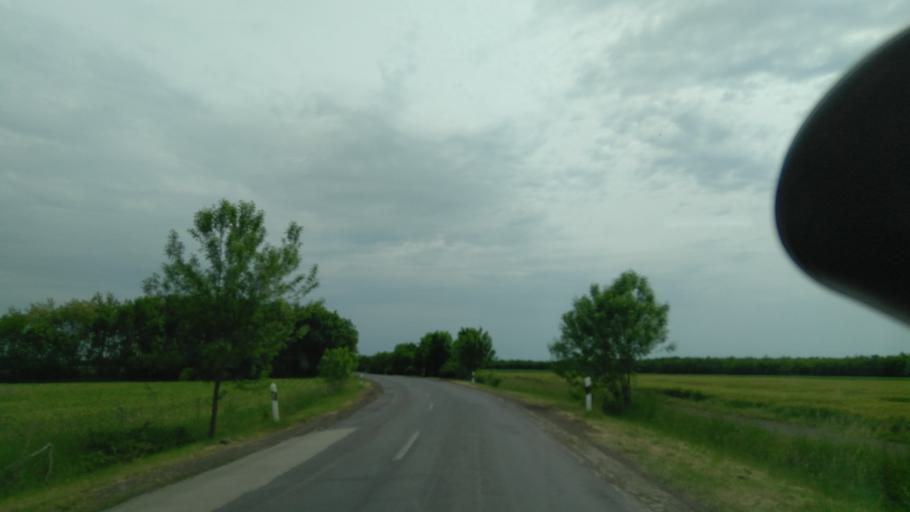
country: HU
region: Bekes
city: Sarkad
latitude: 46.7950
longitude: 21.3801
